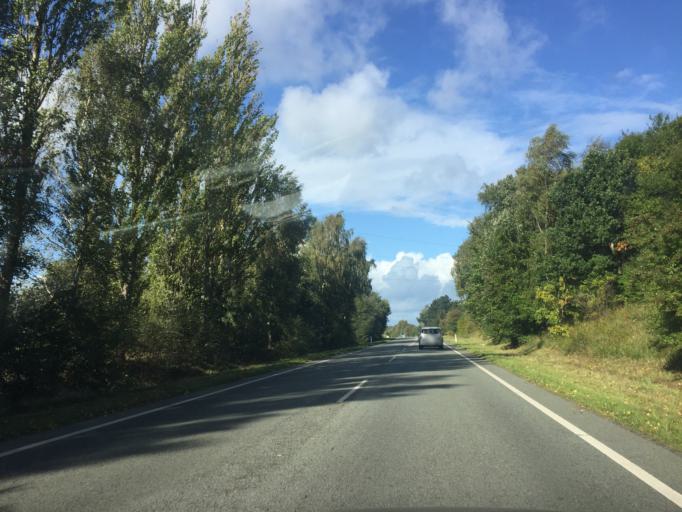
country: DK
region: Capital Region
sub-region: Gribskov Kommune
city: Helsinge
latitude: 56.0284
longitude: 12.1693
